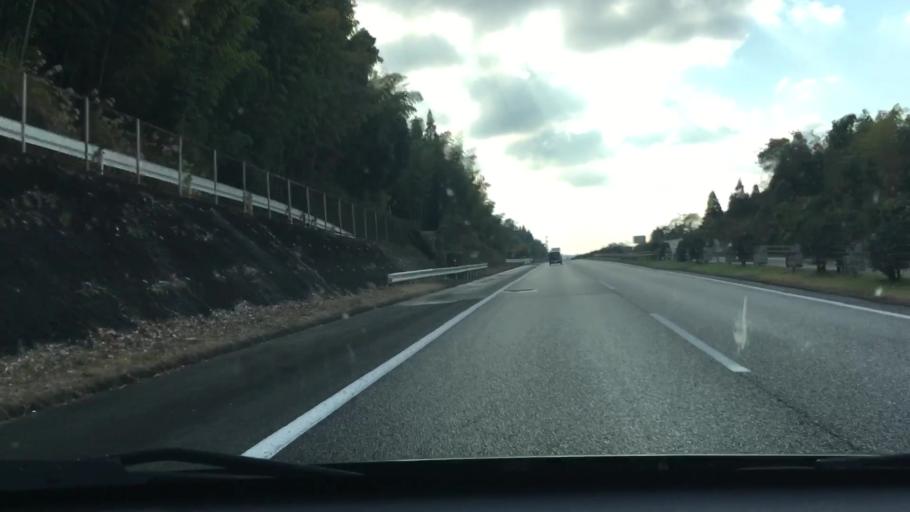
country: JP
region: Kumamoto
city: Yatsushiro
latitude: 32.5306
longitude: 130.6684
